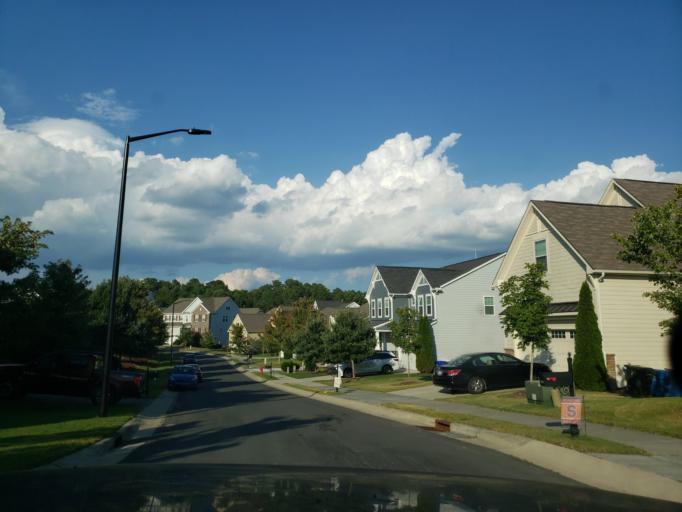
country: US
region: North Carolina
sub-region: Durham County
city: Durham
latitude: 35.9325
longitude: -78.9301
